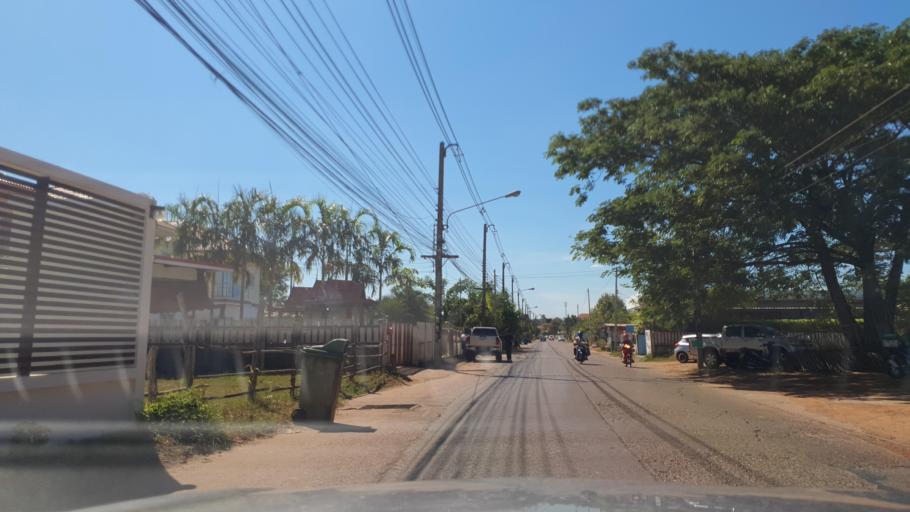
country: TH
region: Sakon Nakhon
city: Sakon Nakhon
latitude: 17.1627
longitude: 104.1230
